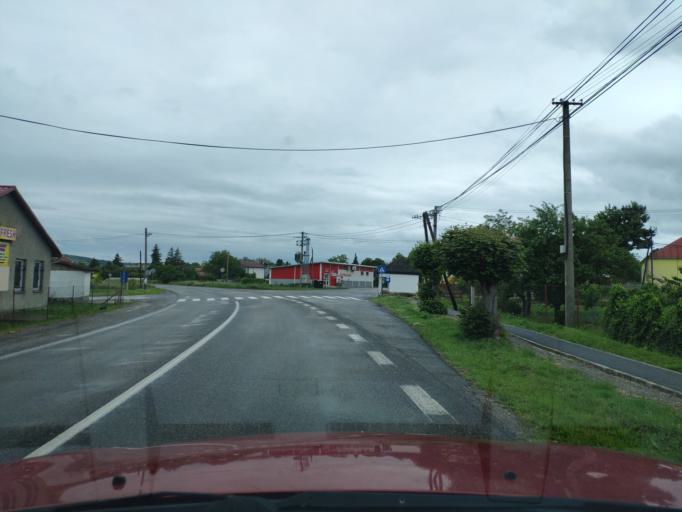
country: HU
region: Borsod-Abauj-Zemplen
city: Karcsa
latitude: 48.4041
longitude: 21.8117
